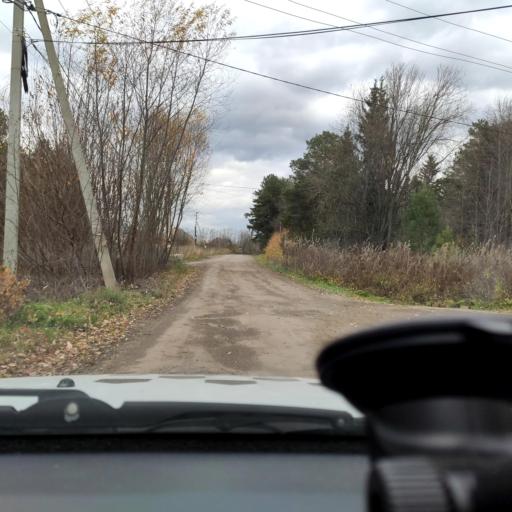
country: RU
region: Perm
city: Perm
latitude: 57.9948
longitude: 56.3325
